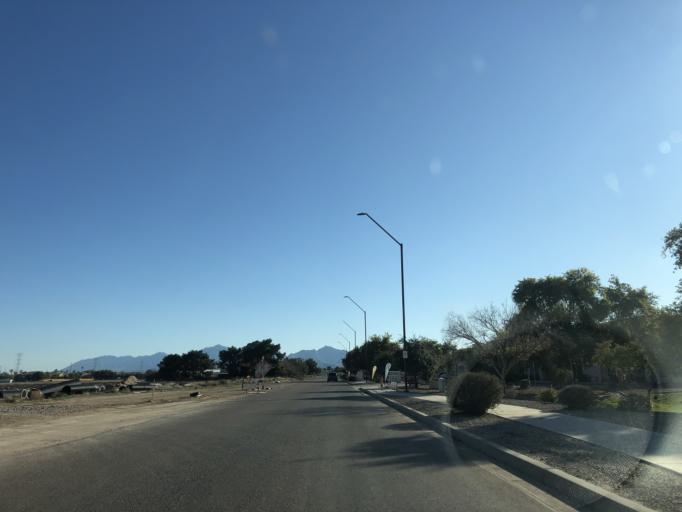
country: US
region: Arizona
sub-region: Maricopa County
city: Avondale
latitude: 33.4546
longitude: -112.3239
